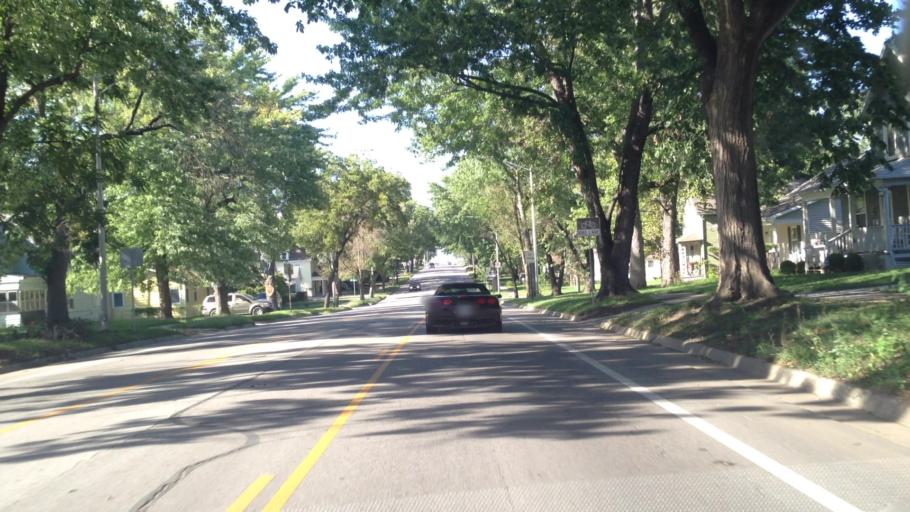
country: US
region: Kansas
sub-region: Franklin County
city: Ottawa
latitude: 38.6265
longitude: -95.2678
